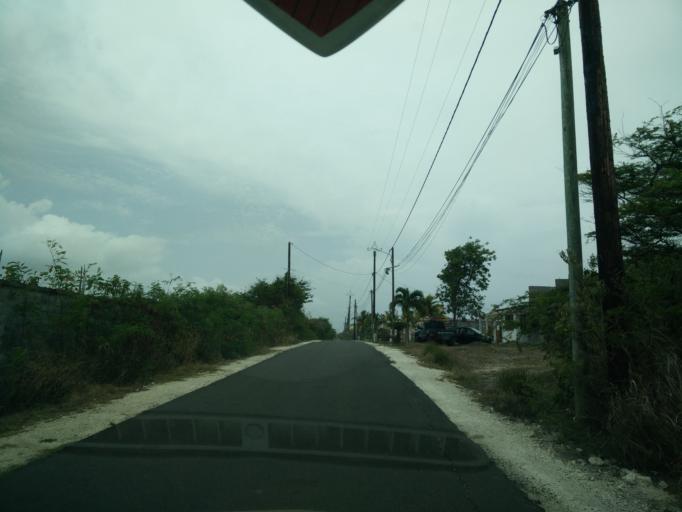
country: GP
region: Guadeloupe
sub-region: Guadeloupe
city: Le Moule
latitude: 16.3199
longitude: -61.2960
